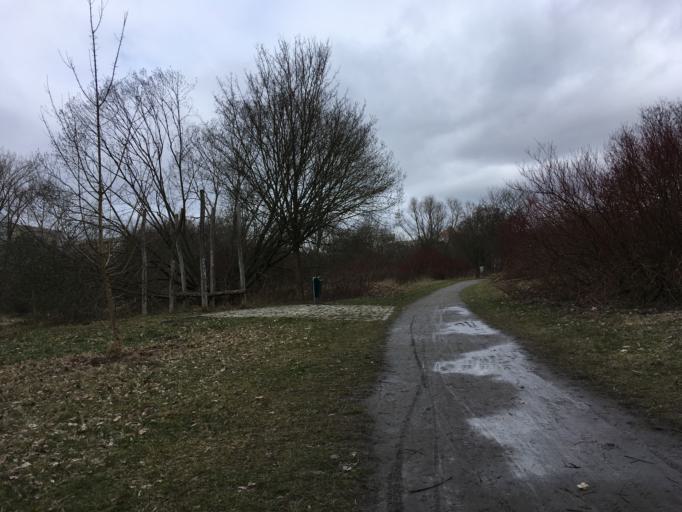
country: DE
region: Berlin
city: Falkenberg
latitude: 52.5630
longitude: 13.5320
